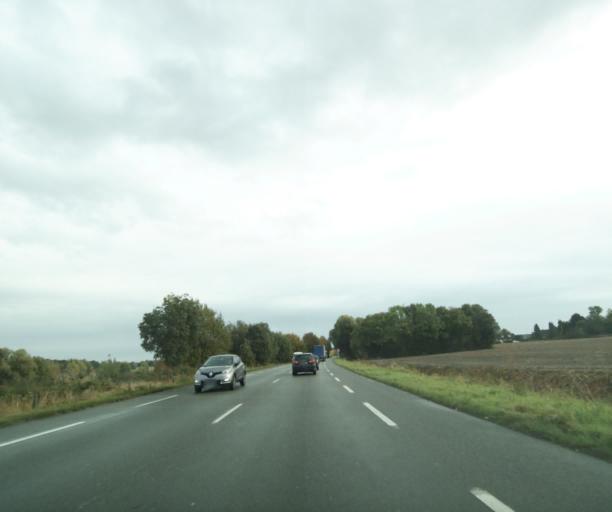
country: FR
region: Nord-Pas-de-Calais
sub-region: Departement du Nord
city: Roncq
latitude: 50.7617
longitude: 3.1307
